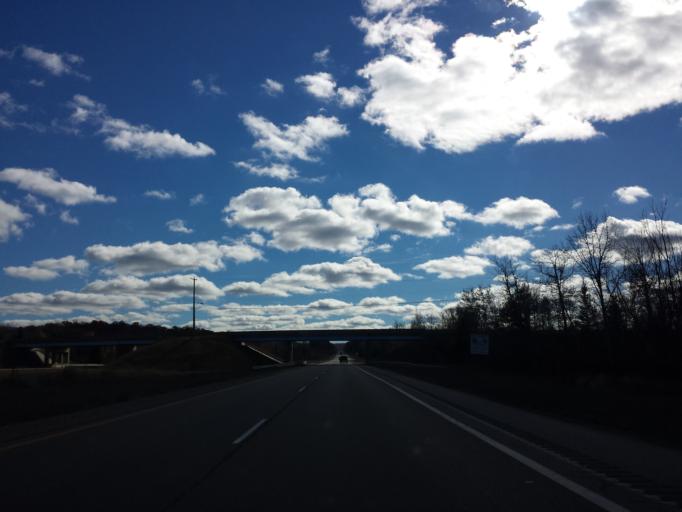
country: US
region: Michigan
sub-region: Cheboygan County
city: Indian River
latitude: 45.4031
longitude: -84.6075
